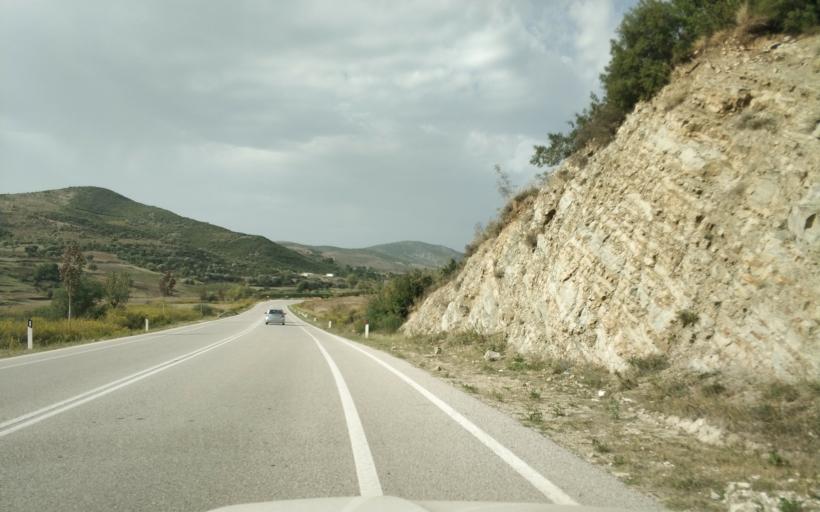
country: AL
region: Gjirokaster
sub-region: Rrethi i Tepelenes
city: Krahes
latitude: 40.4032
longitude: 19.8630
